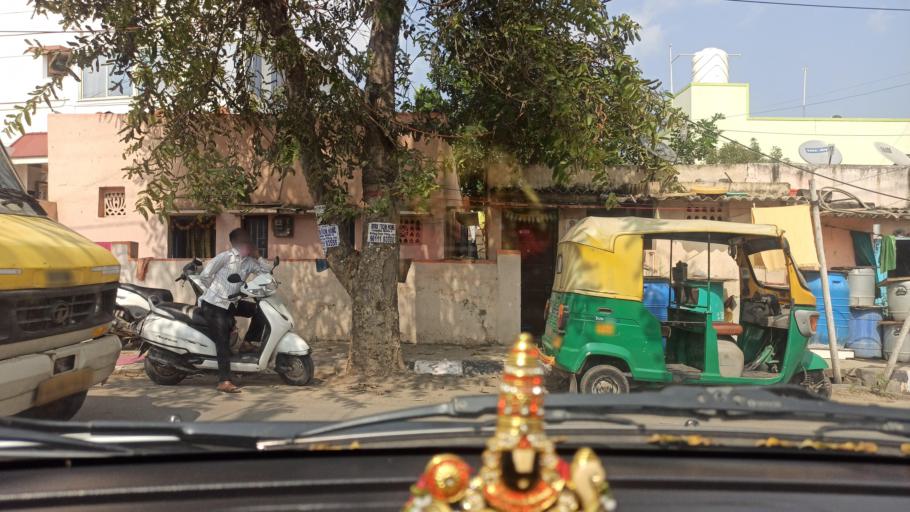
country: IN
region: Karnataka
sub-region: Bangalore Urban
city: Bangalore
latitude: 13.0175
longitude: 77.6705
